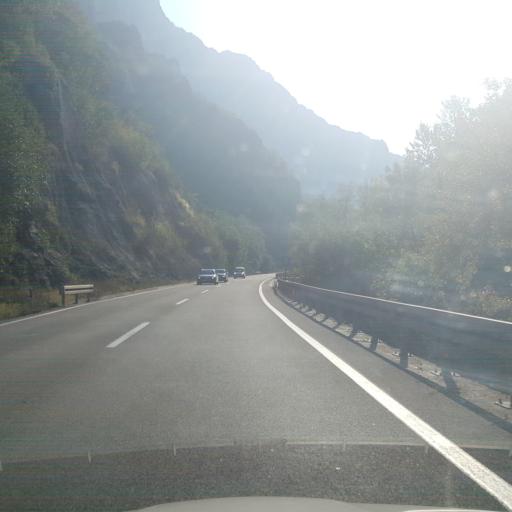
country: RS
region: Central Serbia
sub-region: Nisavski Okrug
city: Svrljig
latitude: 43.3323
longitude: 22.1505
